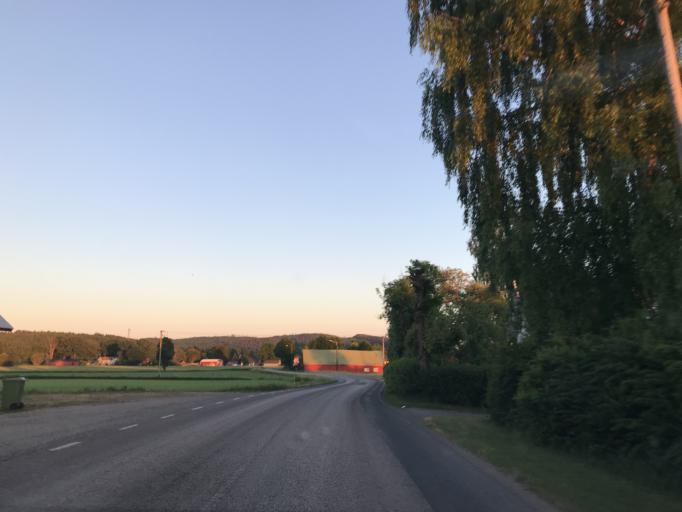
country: SE
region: Vaestra Goetaland
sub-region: Marks Kommun
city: Horred
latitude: 57.4316
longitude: 12.5180
